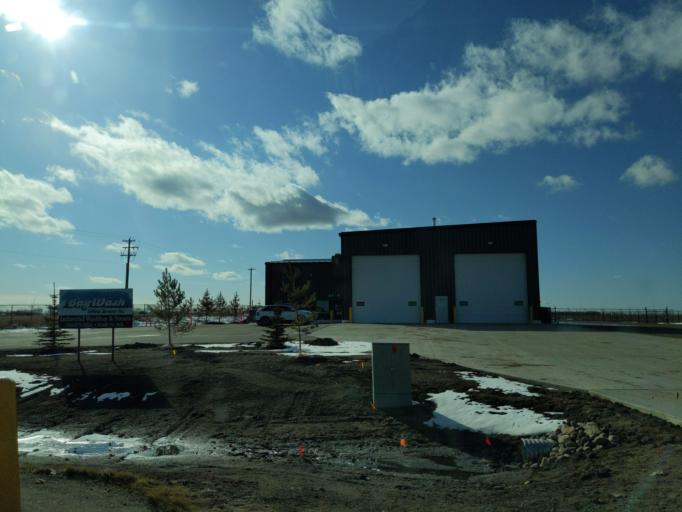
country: CA
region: Saskatchewan
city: Lloydminster
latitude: 53.3017
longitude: -110.0448
